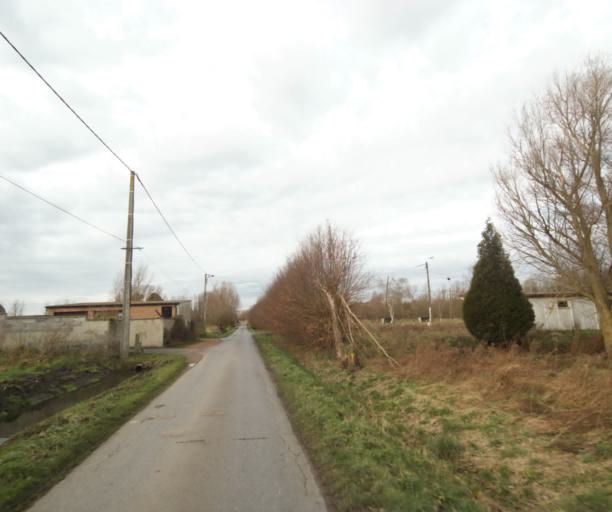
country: FR
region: Nord-Pas-de-Calais
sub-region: Departement du Nord
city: Hergnies
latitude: 50.4937
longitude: 3.5427
